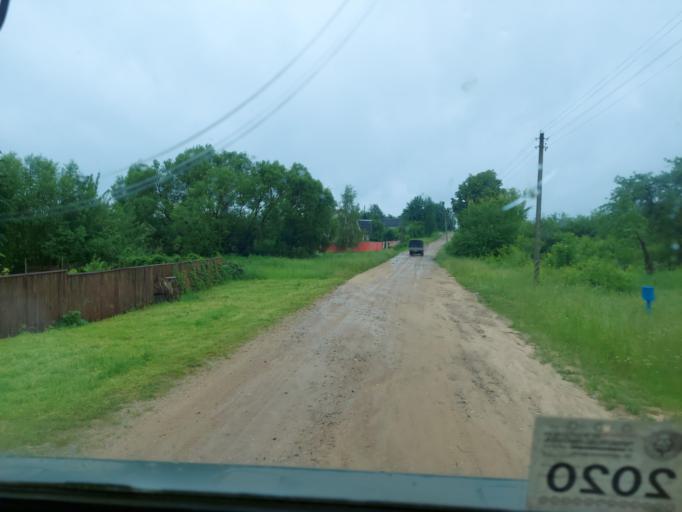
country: BY
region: Mogilev
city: Poselok Voskhod
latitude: 53.6780
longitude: 30.3881
